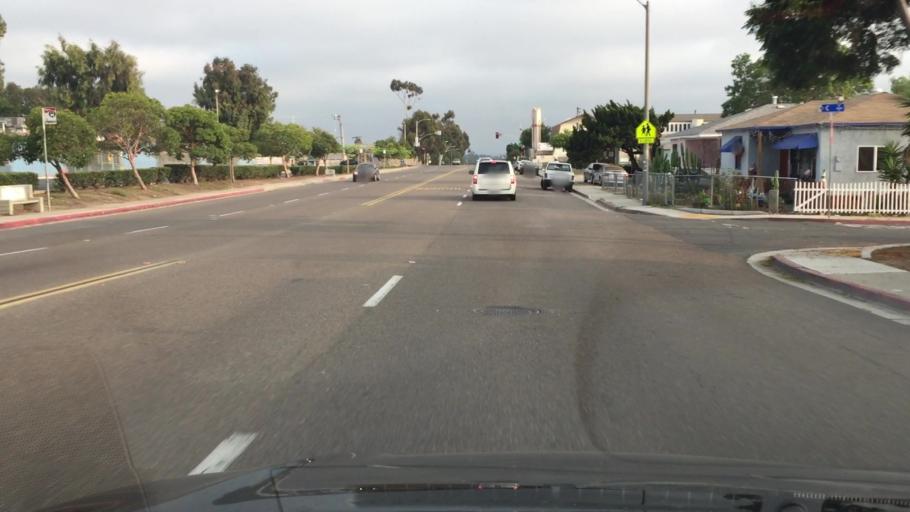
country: US
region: California
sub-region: San Diego County
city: National City
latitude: 32.7169
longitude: -117.0937
